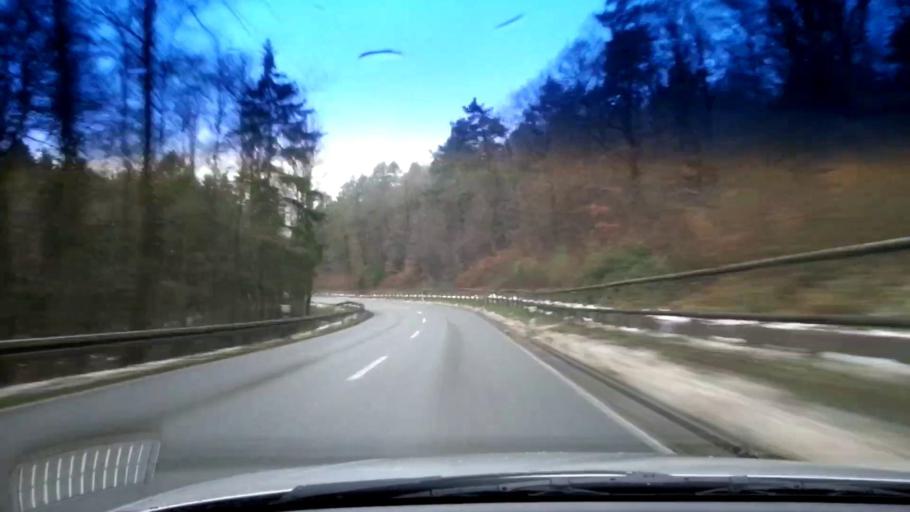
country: DE
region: Bavaria
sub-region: Upper Franconia
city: Gundelsheim
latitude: 49.9638
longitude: 10.9341
